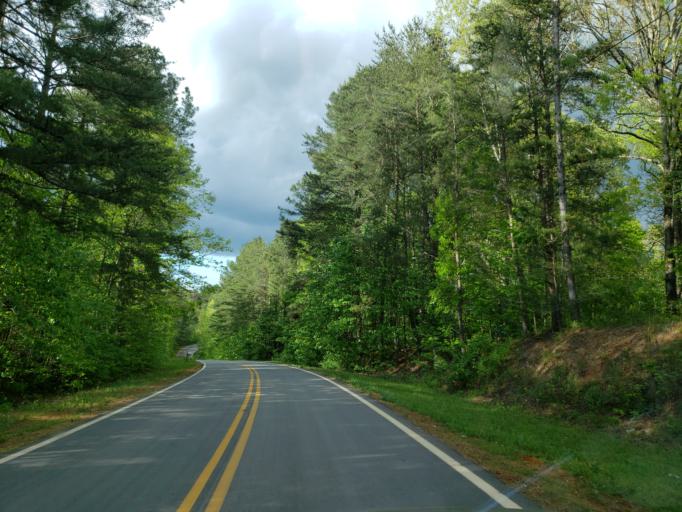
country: US
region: Georgia
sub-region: Haralson County
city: Tallapoosa
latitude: 33.8532
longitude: -85.3728
